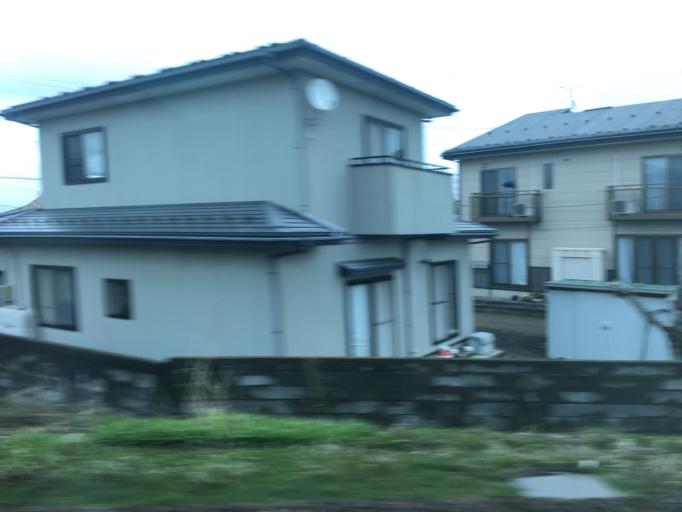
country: JP
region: Akita
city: Akita Shi
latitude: 39.7832
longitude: 140.0672
